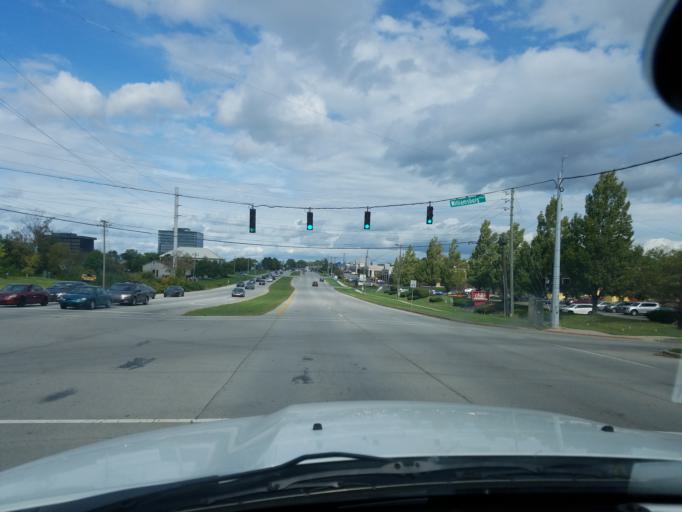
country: US
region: Kentucky
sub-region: Jefferson County
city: Hurstbourne
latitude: 38.2396
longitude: -85.5769
